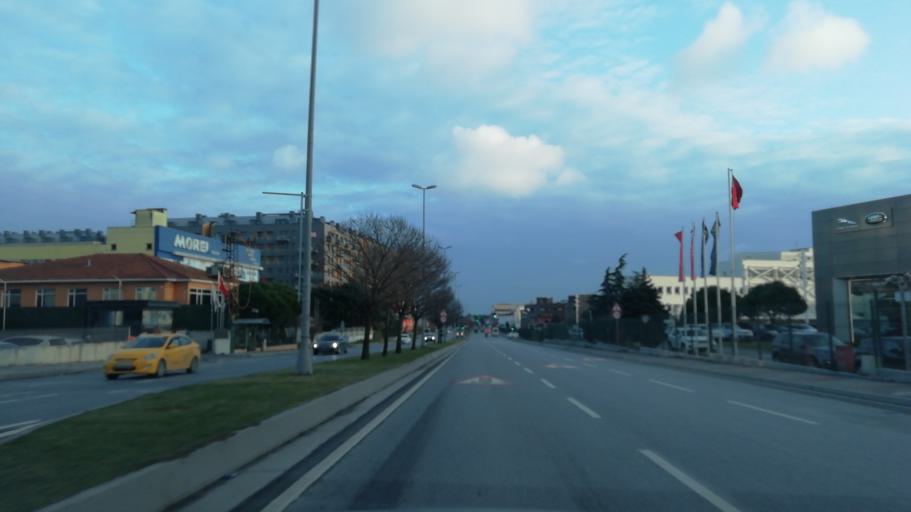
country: TR
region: Istanbul
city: Yakuplu
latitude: 40.9941
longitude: 28.7163
